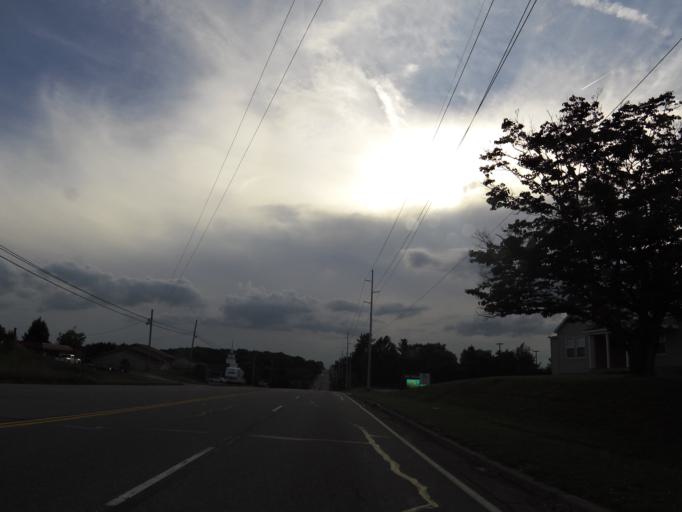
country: US
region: Tennessee
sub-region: Blount County
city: Wildwood
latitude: 35.7577
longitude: -83.8918
